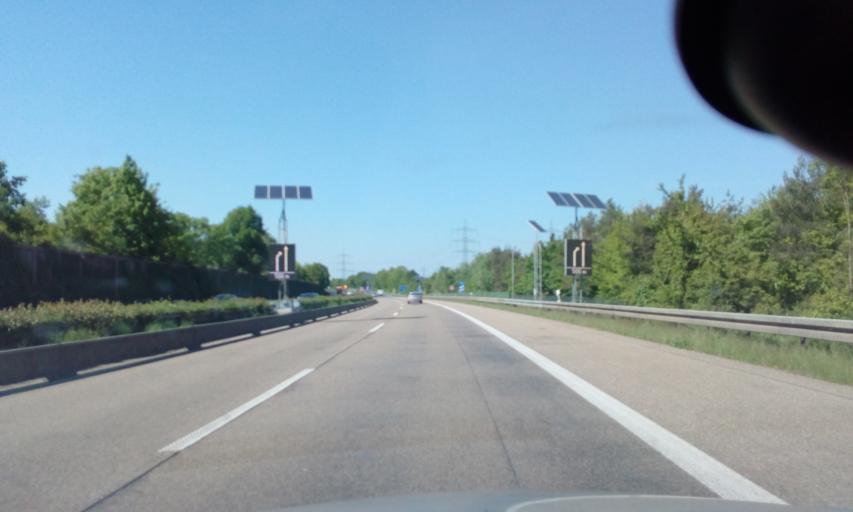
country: DE
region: North Rhine-Westphalia
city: Bruhl
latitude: 50.8237
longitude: 6.9340
